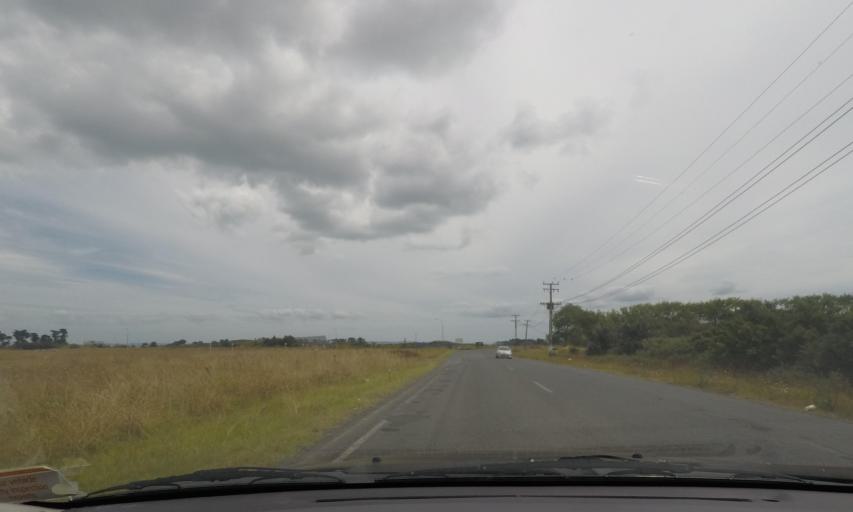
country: NZ
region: Auckland
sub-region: Auckland
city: Mangere
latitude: -36.9952
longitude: 174.7799
